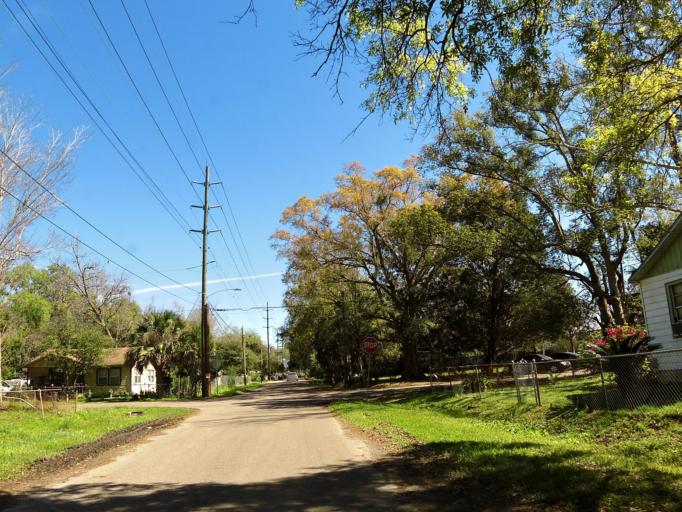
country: US
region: Florida
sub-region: Duval County
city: Jacksonville
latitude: 30.3226
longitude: -81.7160
